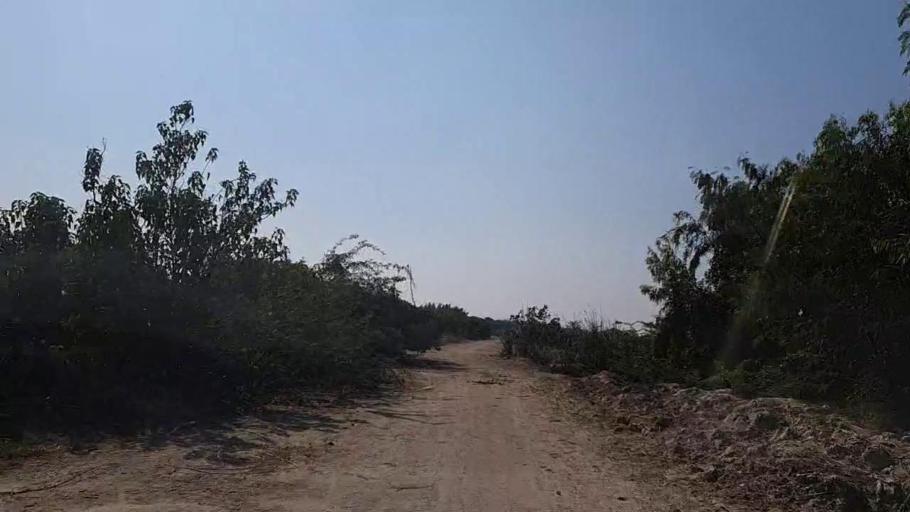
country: PK
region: Sindh
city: Thatta
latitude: 24.7877
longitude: 67.9366
